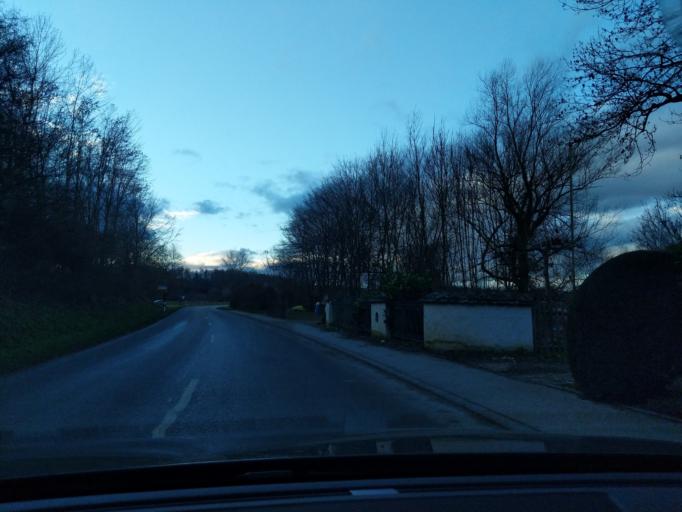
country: DE
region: Baden-Wuerttemberg
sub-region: Tuebingen Region
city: Salem
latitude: 47.7467
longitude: 9.2979
